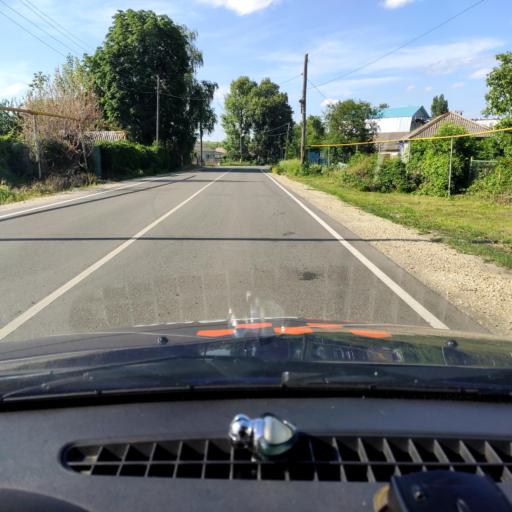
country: RU
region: Voronezj
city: Devitsa
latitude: 51.6558
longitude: 38.9704
